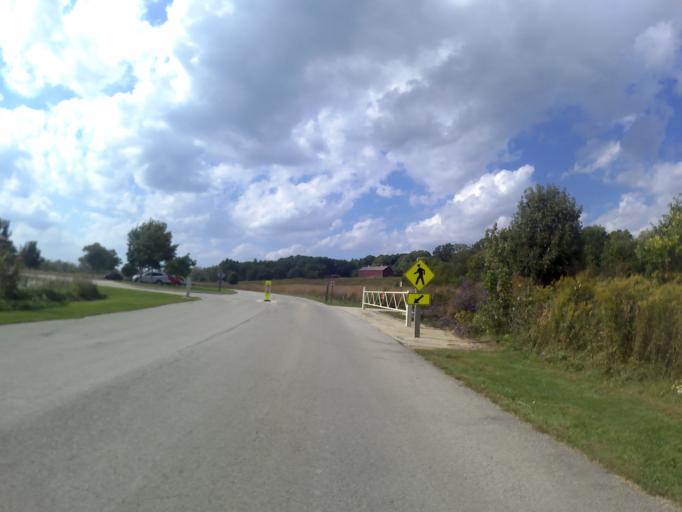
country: US
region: Illinois
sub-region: Will County
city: Bolingbrook
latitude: 41.7165
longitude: -88.1000
